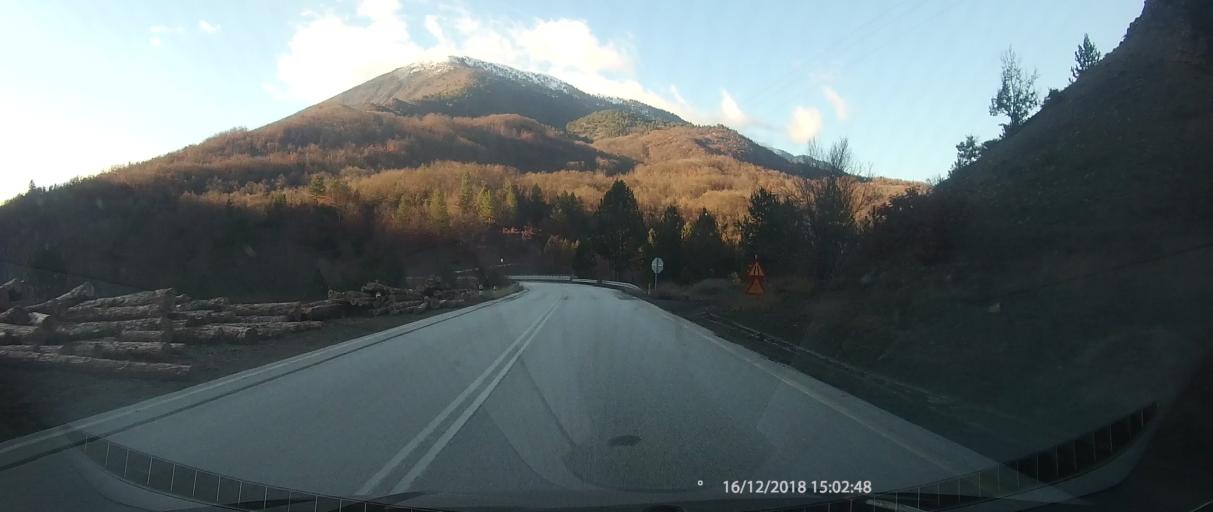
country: GR
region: West Macedonia
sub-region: Nomos Kastorias
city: Nestorio
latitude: 40.2302
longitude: 20.9903
